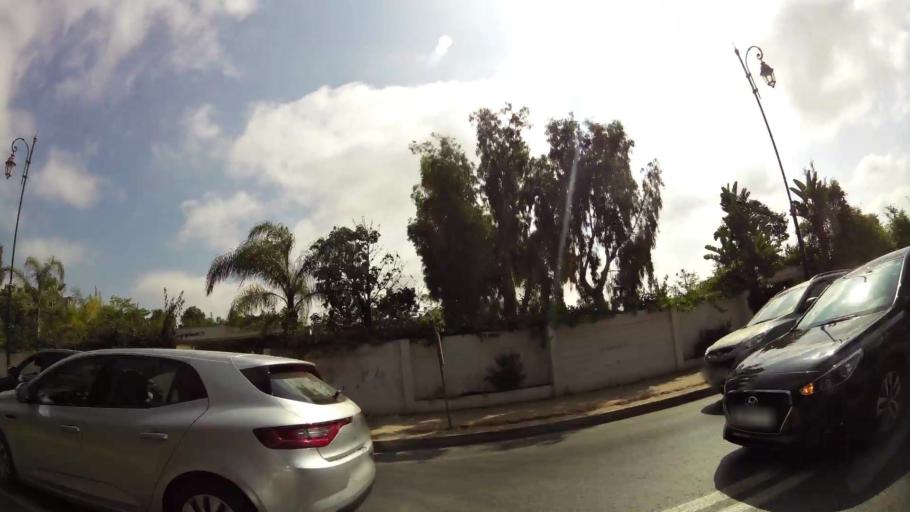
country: MA
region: Rabat-Sale-Zemmour-Zaer
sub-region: Rabat
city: Rabat
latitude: 33.9800
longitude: -6.8428
